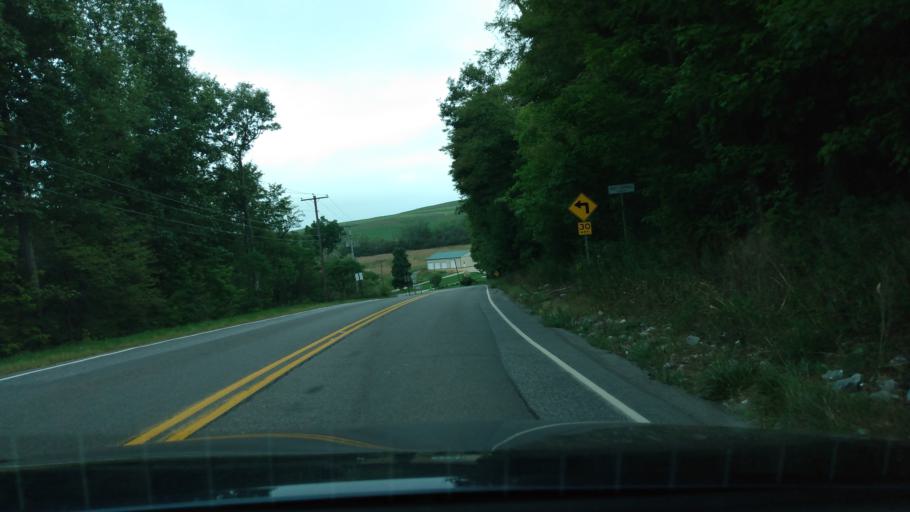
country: US
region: Pennsylvania
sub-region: Cambria County
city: Hastings
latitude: 40.6142
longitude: -78.7121
